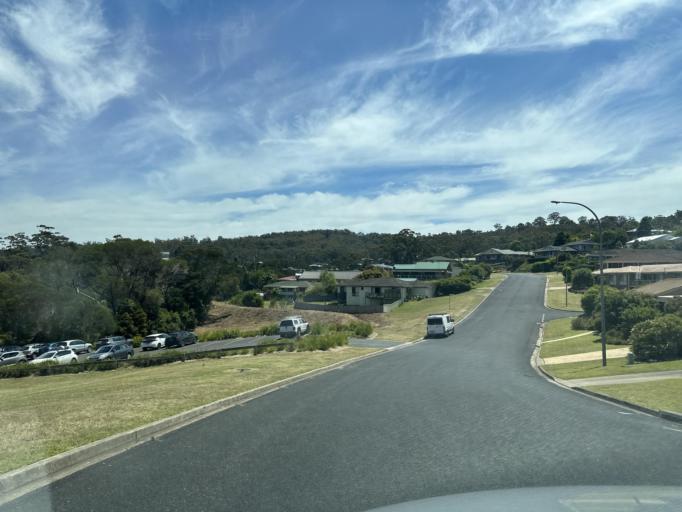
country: AU
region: New South Wales
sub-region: Bega Valley
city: Merimbula
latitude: -36.8915
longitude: 149.8929
